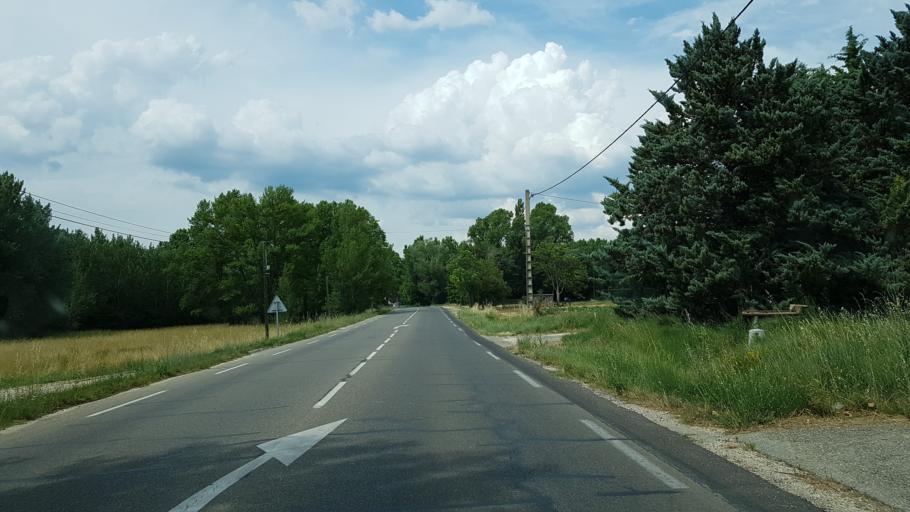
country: FR
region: Provence-Alpes-Cote d'Azur
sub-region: Departement du Vaucluse
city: Apt
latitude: 43.8981
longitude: 5.3832
